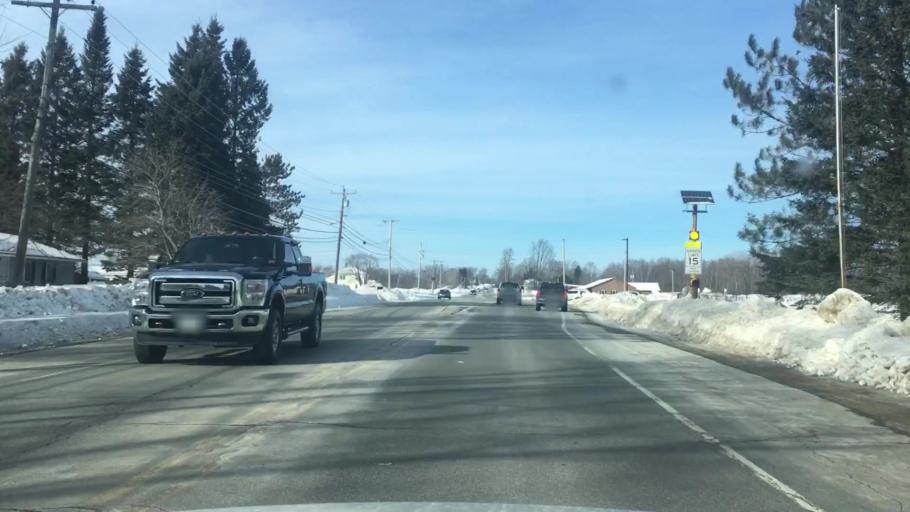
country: US
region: Maine
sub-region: Penobscot County
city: Charleston
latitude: 45.0155
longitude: -69.0275
